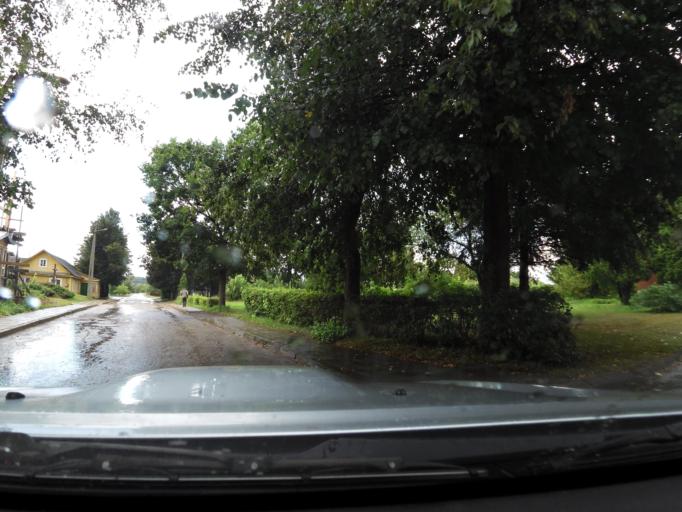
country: LT
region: Vilnius County
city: Ukmerge
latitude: 55.2943
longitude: 24.5052
